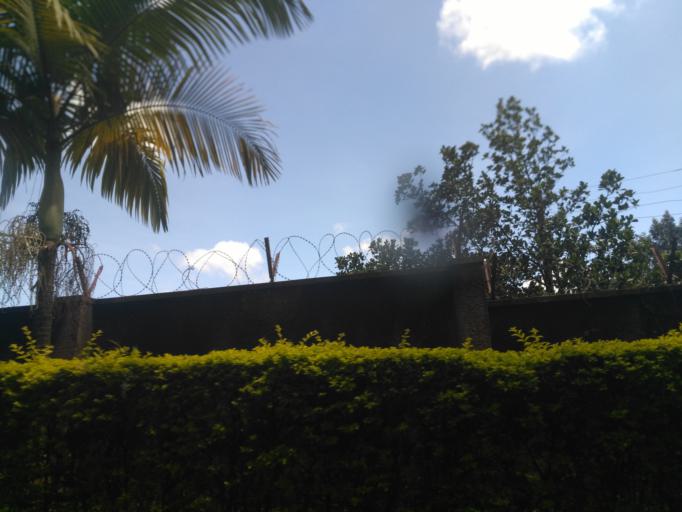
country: UG
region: Central Region
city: Kampala Central Division
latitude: 0.3262
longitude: 32.5793
